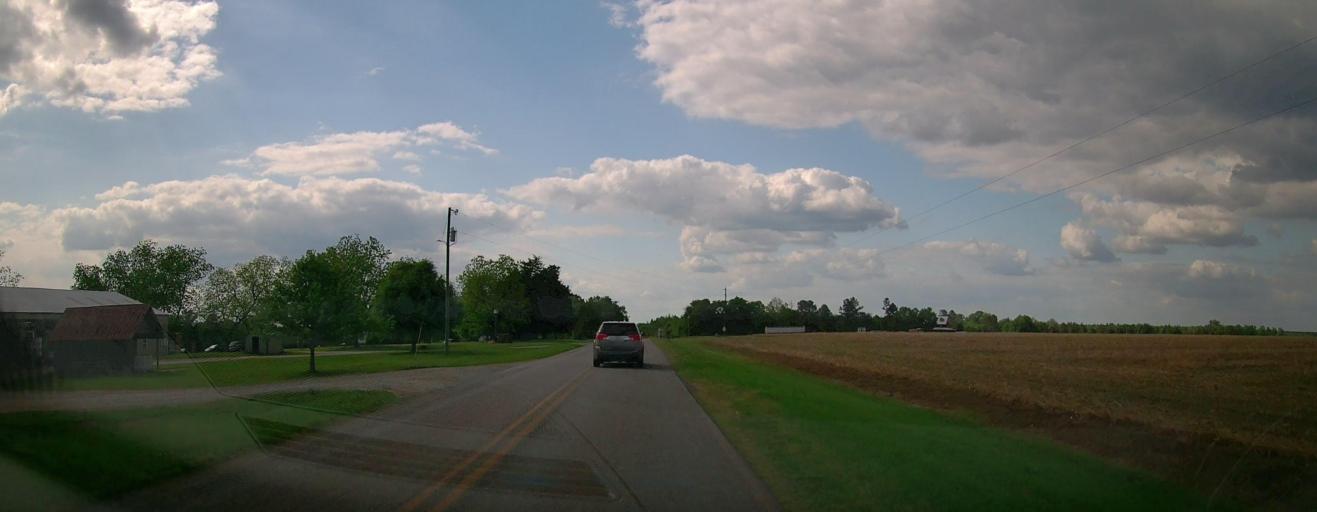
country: US
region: Georgia
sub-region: Laurens County
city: East Dublin
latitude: 32.6860
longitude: -82.8946
